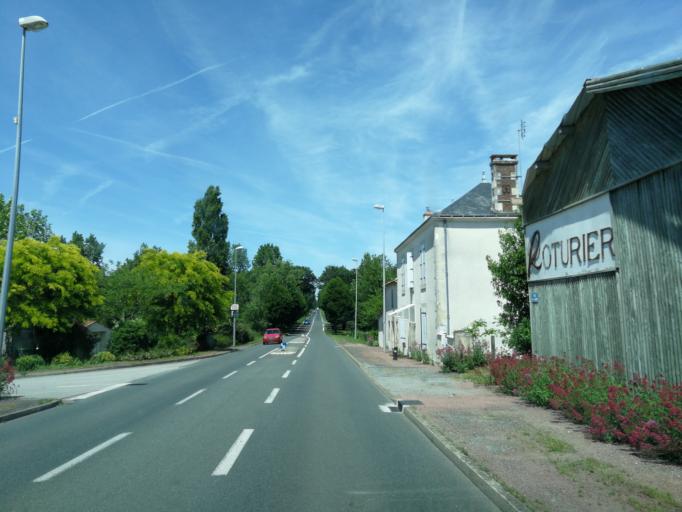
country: FR
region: Pays de la Loire
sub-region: Departement de la Vendee
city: Pissotte
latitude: 46.5327
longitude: -0.8074
